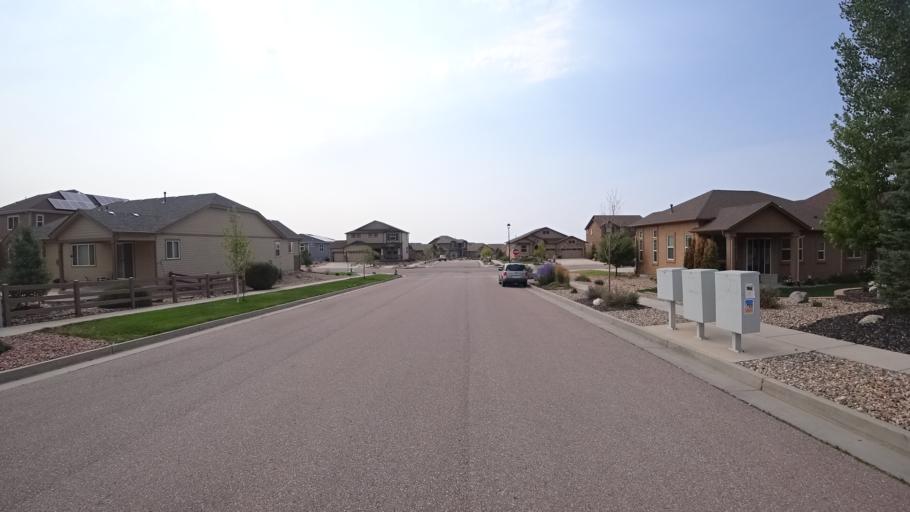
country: US
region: Colorado
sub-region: El Paso County
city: Black Forest
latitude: 38.9661
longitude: -104.7172
